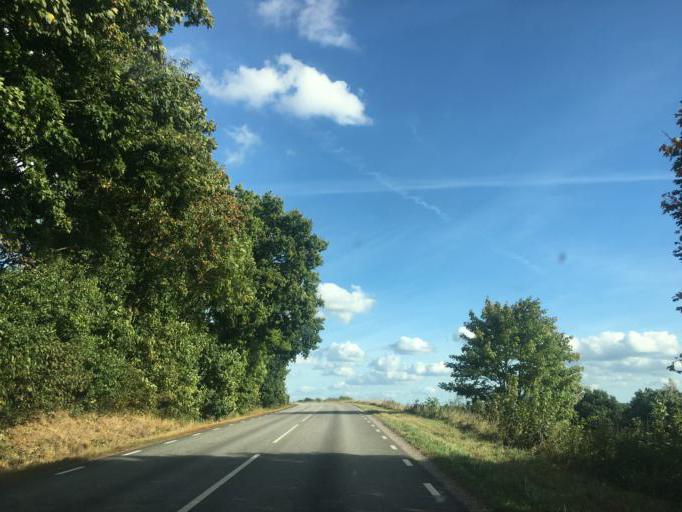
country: SE
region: Skane
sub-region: Hoors Kommun
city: Loberod
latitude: 55.7289
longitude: 13.4825
